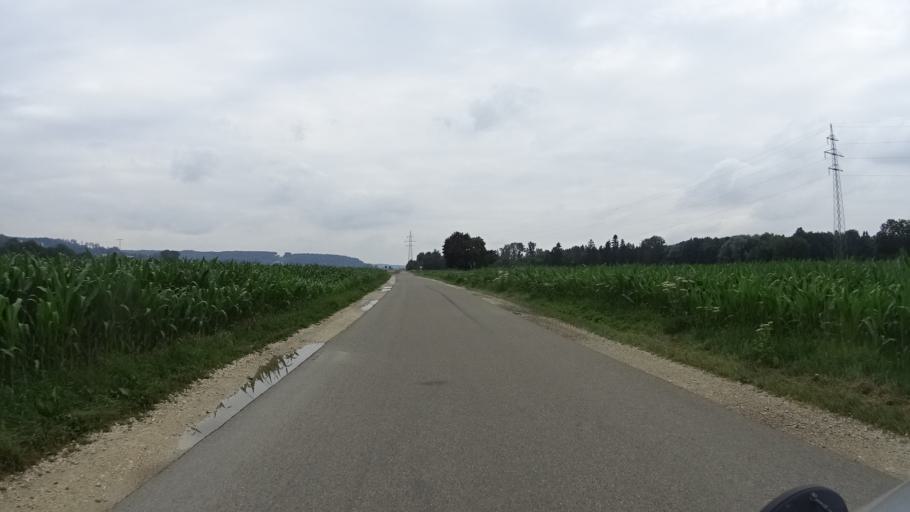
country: DE
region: Bavaria
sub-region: Swabia
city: Altenstadt
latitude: 48.1544
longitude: 10.0954
